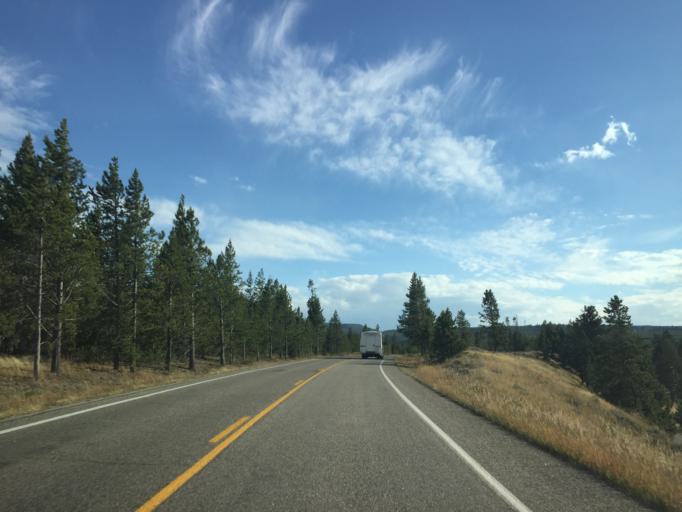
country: US
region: Montana
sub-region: Gallatin County
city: West Yellowstone
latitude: 44.6590
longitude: -110.9905
